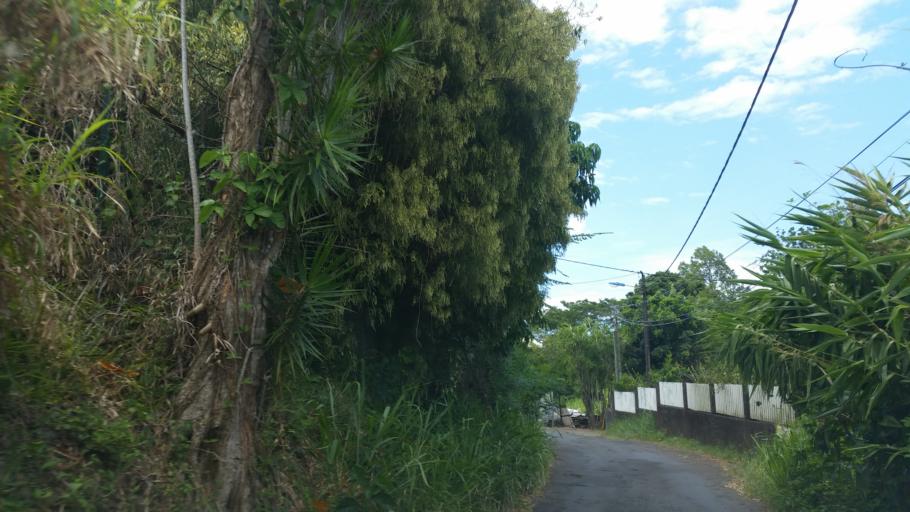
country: RE
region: Reunion
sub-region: Reunion
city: Sainte-Marie
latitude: -20.9283
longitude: 55.5220
